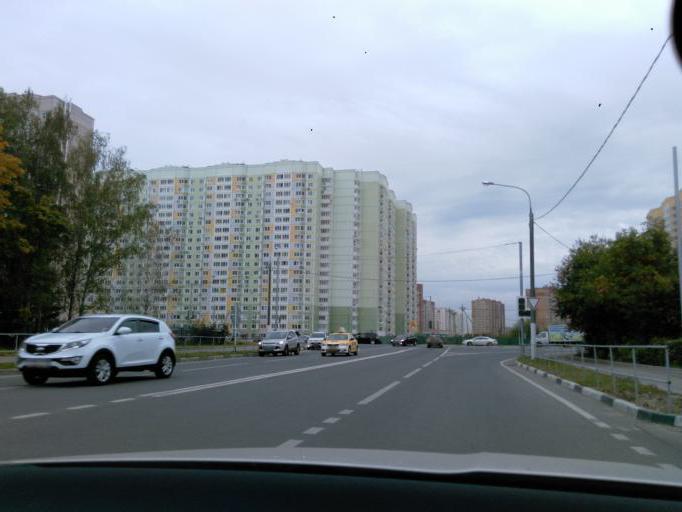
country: RU
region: Moskovskaya
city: Dolgoprudnyy
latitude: 55.9314
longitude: 37.5023
